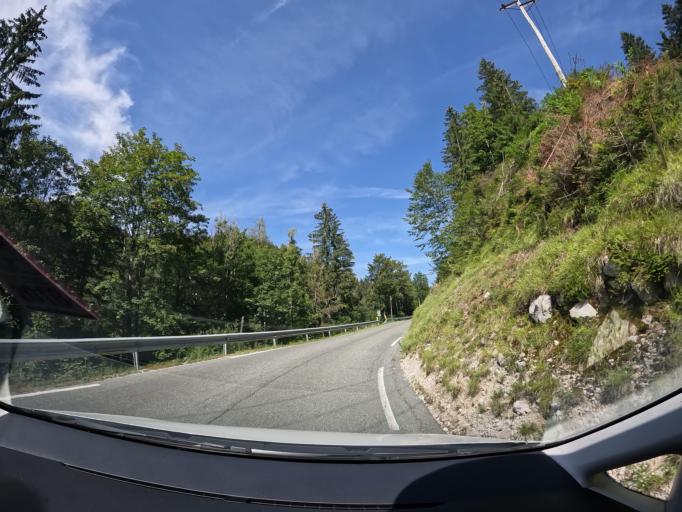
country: AT
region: Carinthia
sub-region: Politischer Bezirk Villach Land
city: Sankt Jakob
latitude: 46.5574
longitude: 14.0774
